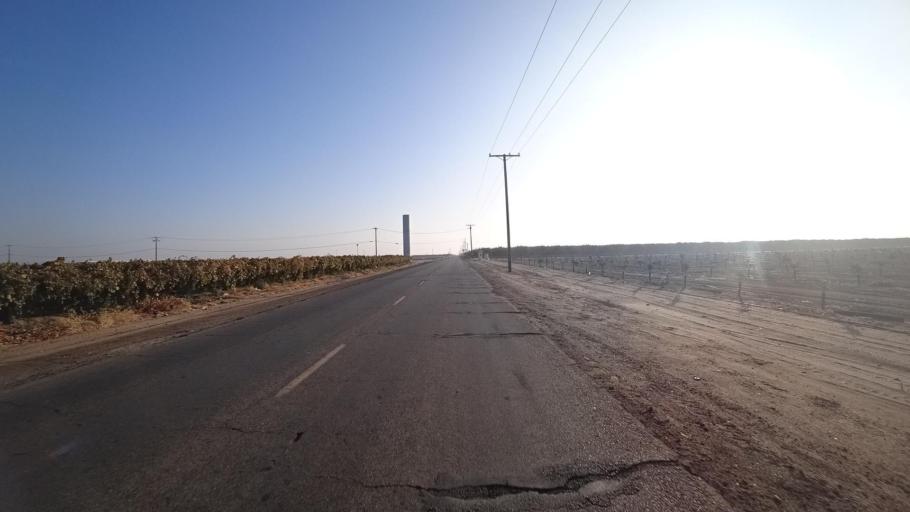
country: US
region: California
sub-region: Tulare County
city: Richgrove
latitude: 35.7906
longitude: -119.1535
